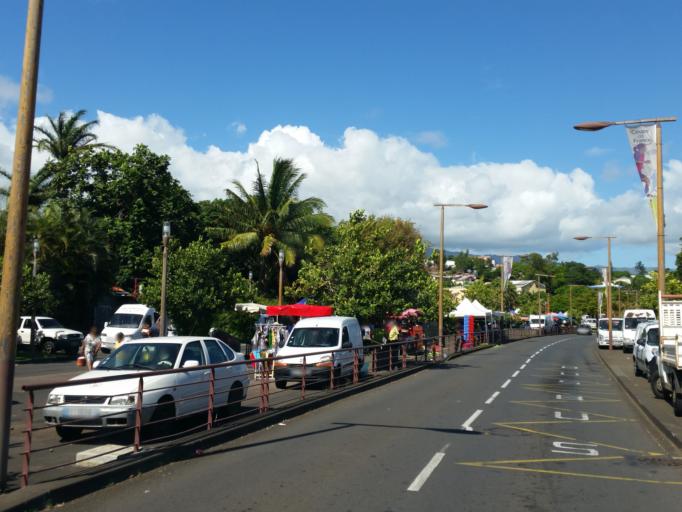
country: RE
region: Reunion
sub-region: Reunion
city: Sainte-Marie
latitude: -20.8960
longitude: 55.5503
